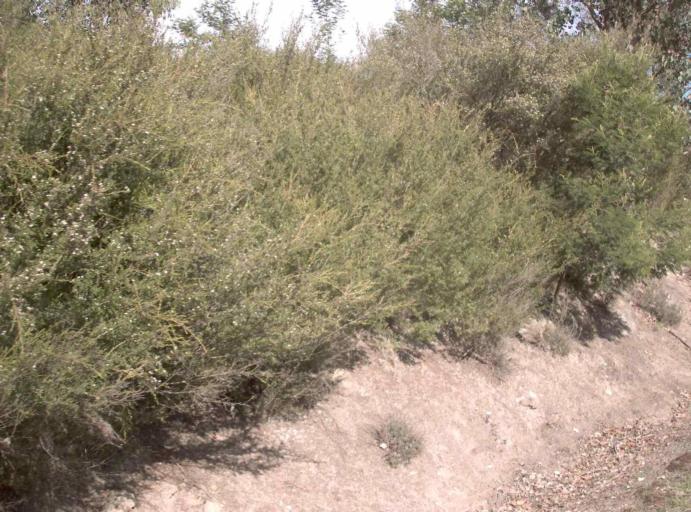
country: AU
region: Victoria
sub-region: East Gippsland
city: Lakes Entrance
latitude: -37.4938
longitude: 148.1321
